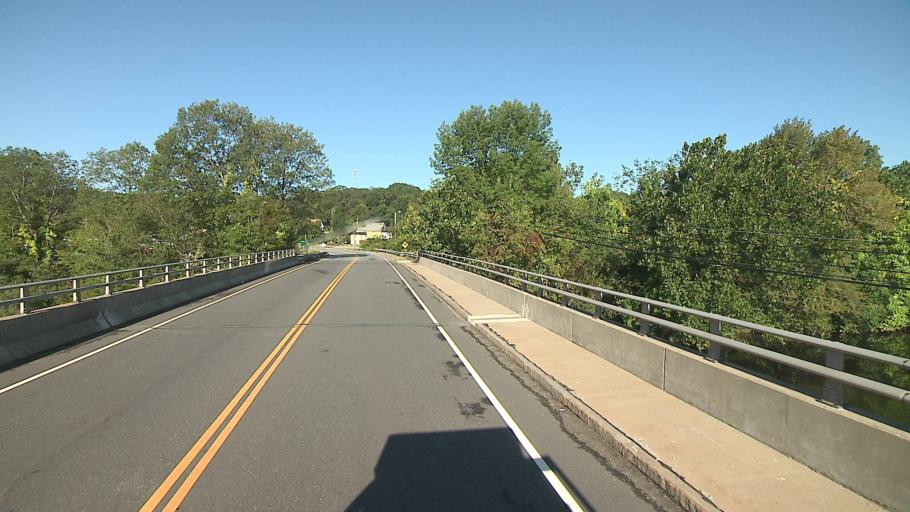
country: US
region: Connecticut
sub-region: New London County
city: Norwich
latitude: 41.5581
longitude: -72.0453
